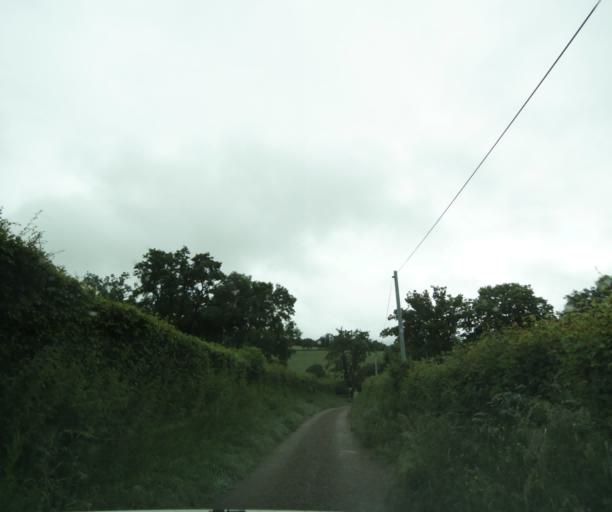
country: FR
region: Bourgogne
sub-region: Departement de Saone-et-Loire
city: La Clayette
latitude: 46.3464
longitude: 4.2138
